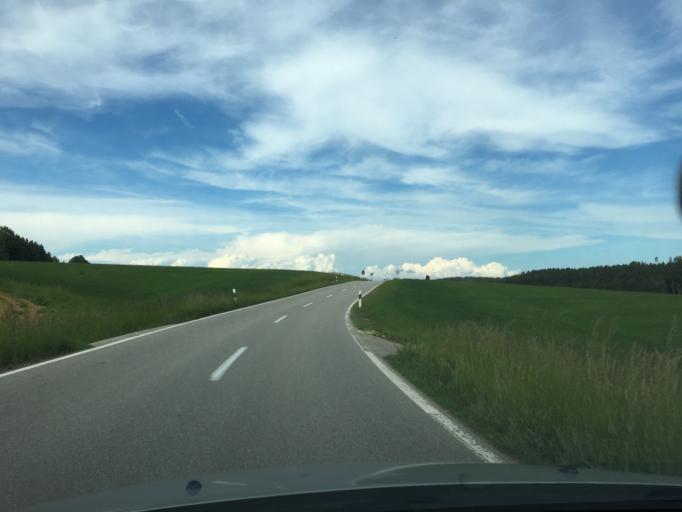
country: DE
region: Bavaria
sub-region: Lower Bavaria
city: Massing
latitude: 48.3648
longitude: 12.5880
